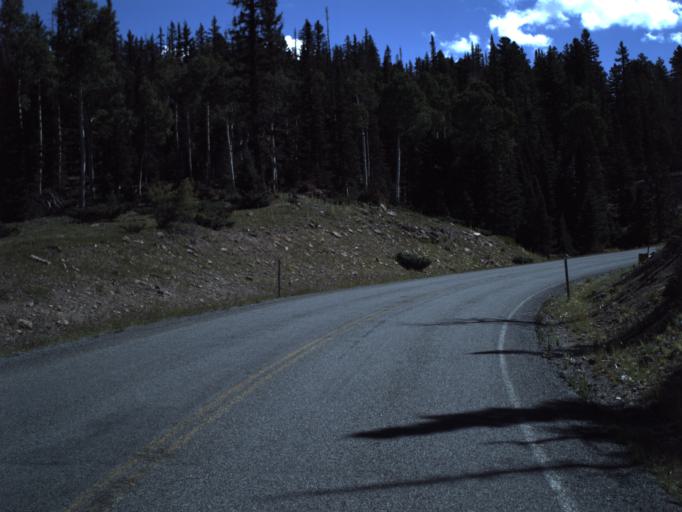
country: US
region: Utah
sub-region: Piute County
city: Junction
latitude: 38.3127
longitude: -112.3993
